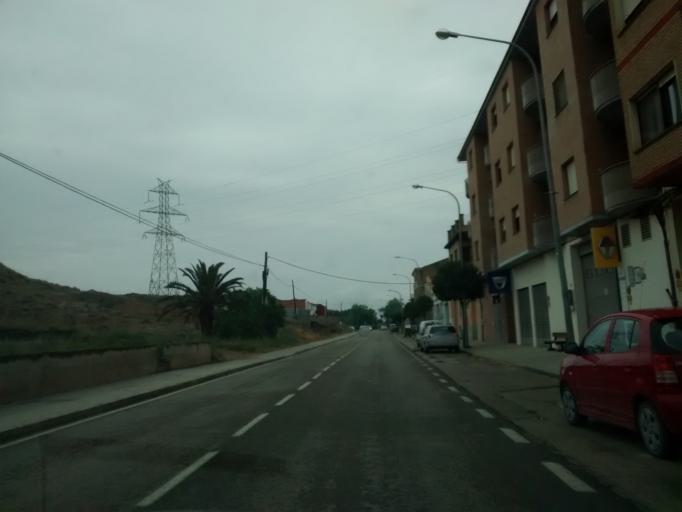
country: ES
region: Aragon
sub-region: Provincia de Zaragoza
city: Caspe
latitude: 41.2282
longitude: -0.0355
